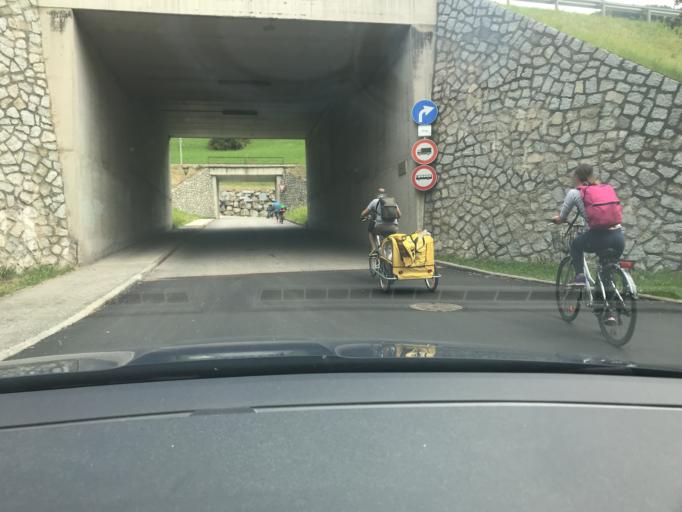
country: IT
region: Trentino-Alto Adige
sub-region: Bolzano
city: San Candido
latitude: 46.7352
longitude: 12.2868
